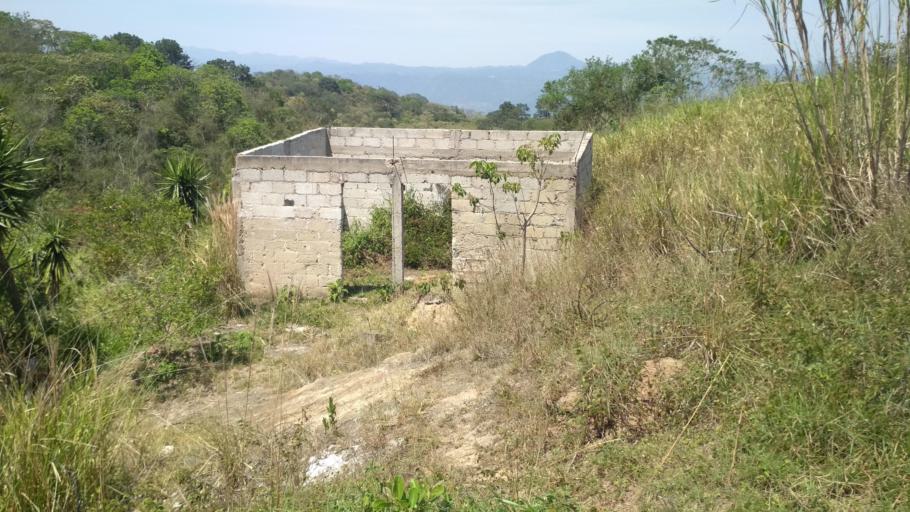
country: MX
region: Veracruz
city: El Castillo
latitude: 19.5513
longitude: -96.8402
